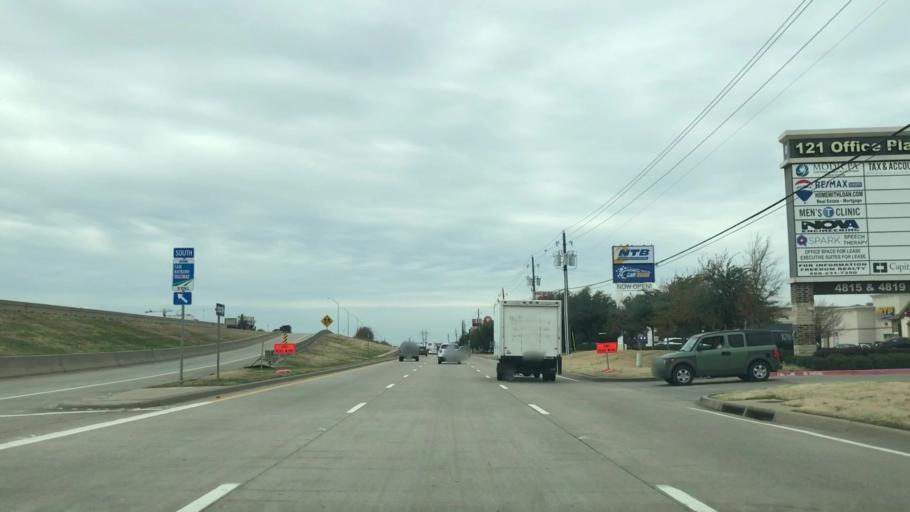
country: US
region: Texas
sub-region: Denton County
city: The Colony
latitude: 33.0681
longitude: -96.8849
